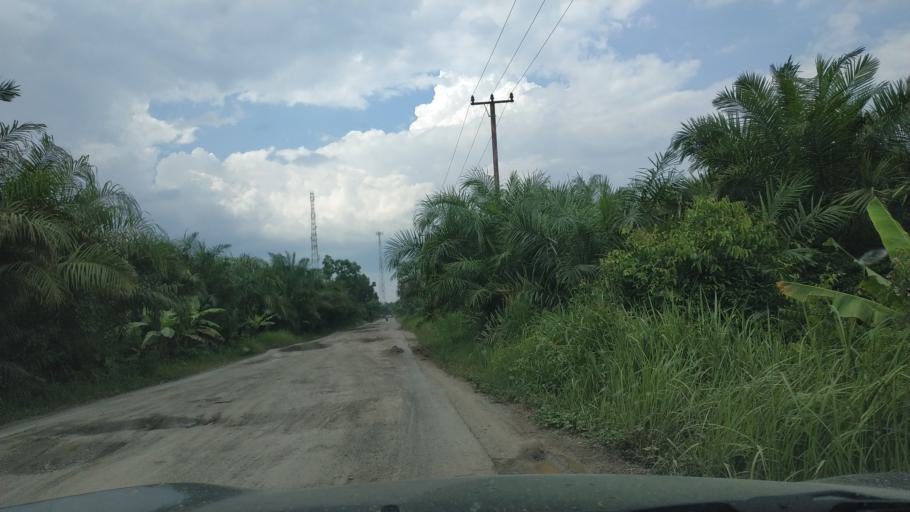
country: ID
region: Riau
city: Sungaisalak
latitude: -0.5233
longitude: 103.0039
